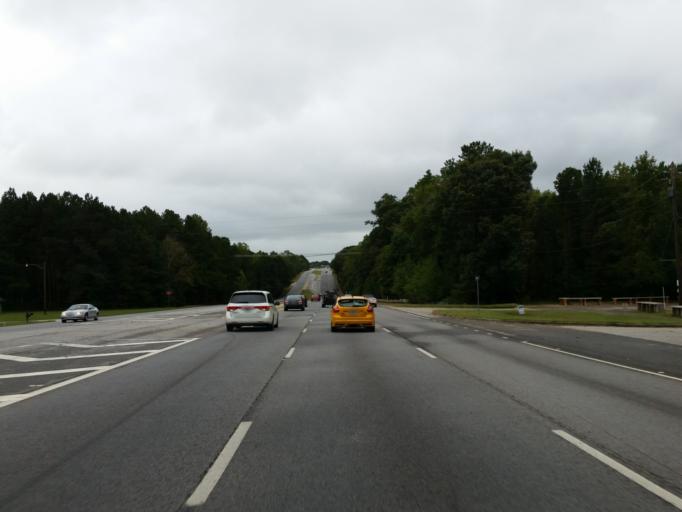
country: US
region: Georgia
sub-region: Henry County
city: Hampton
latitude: 33.3641
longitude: -84.2963
